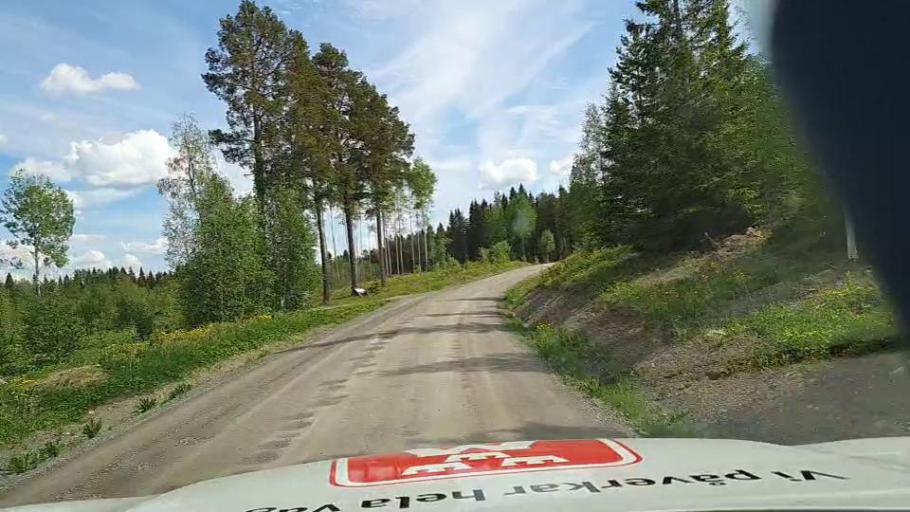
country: SE
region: Jaemtland
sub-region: OEstersunds Kommun
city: Brunflo
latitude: 63.0070
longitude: 14.7910
